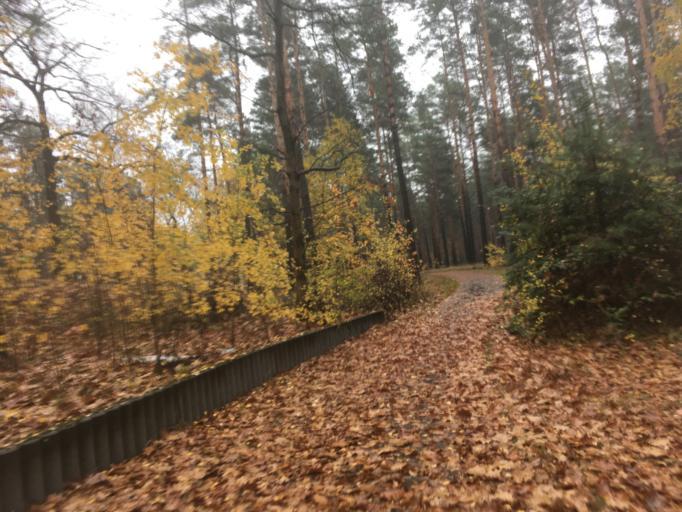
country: DE
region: Brandenburg
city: Schlepzig
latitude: 52.0312
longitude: 13.7971
